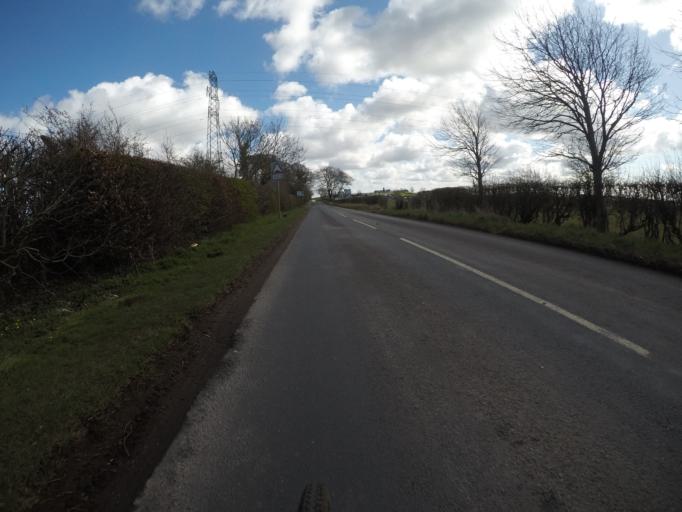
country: GB
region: Scotland
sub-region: North Ayrshire
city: Dreghorn
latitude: 55.5950
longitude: -4.6102
